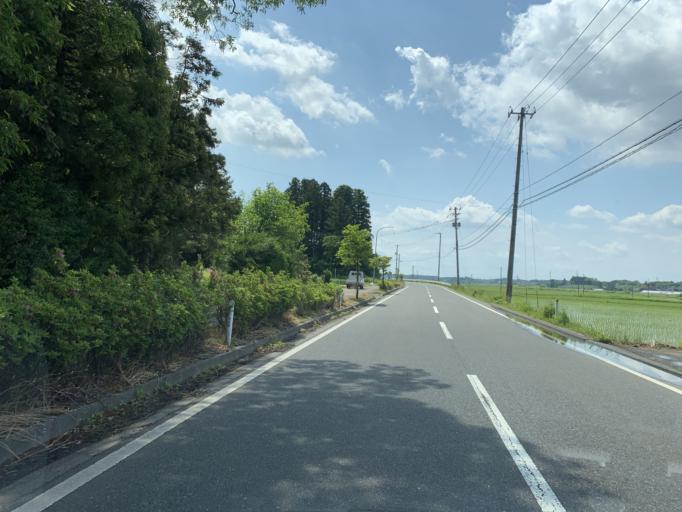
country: JP
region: Miyagi
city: Furukawa
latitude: 38.6713
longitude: 140.9934
